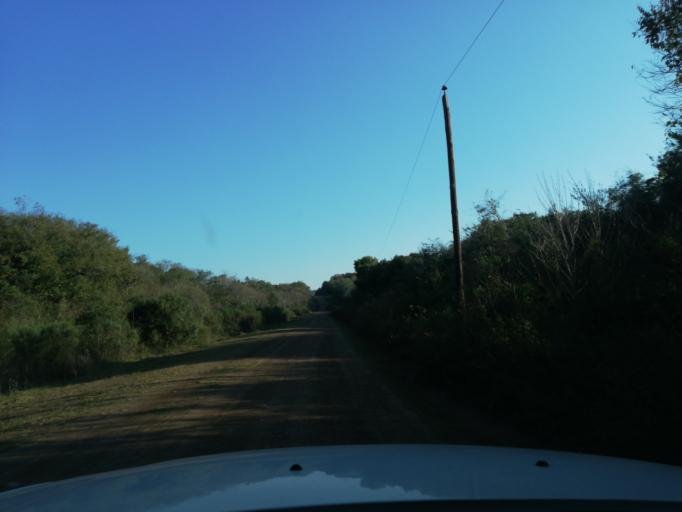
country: AR
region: Misiones
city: Cerro Cora
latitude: -27.5913
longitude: -55.6922
